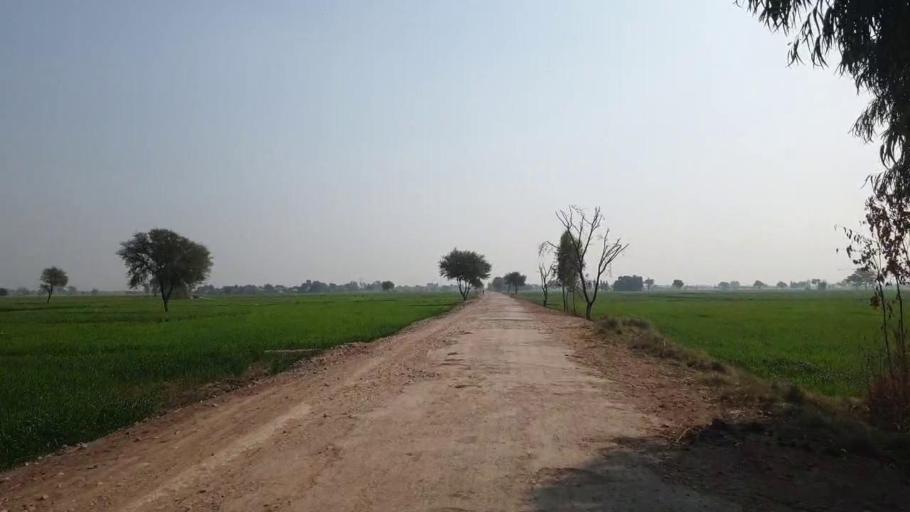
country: PK
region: Sindh
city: Bhit Shah
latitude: 25.7352
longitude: 68.5256
